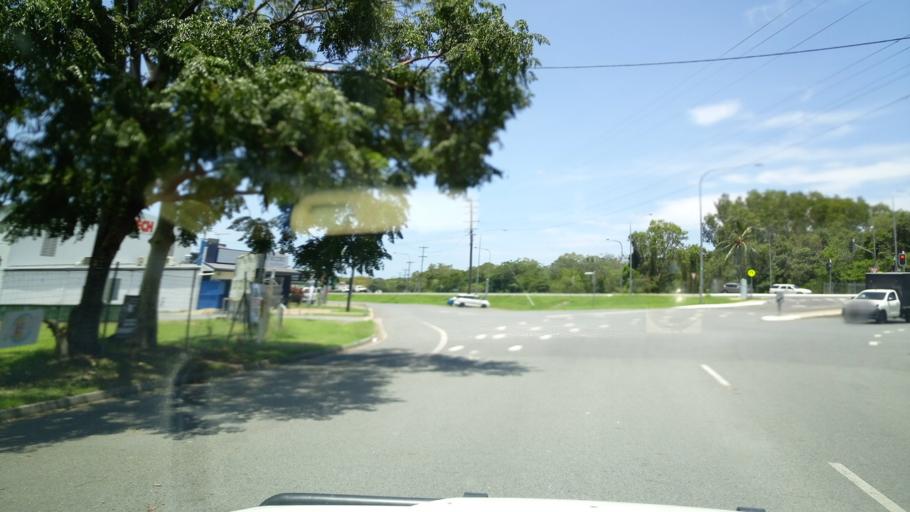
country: AU
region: Queensland
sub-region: Cairns
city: Redlynch
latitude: -16.8739
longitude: 145.7398
